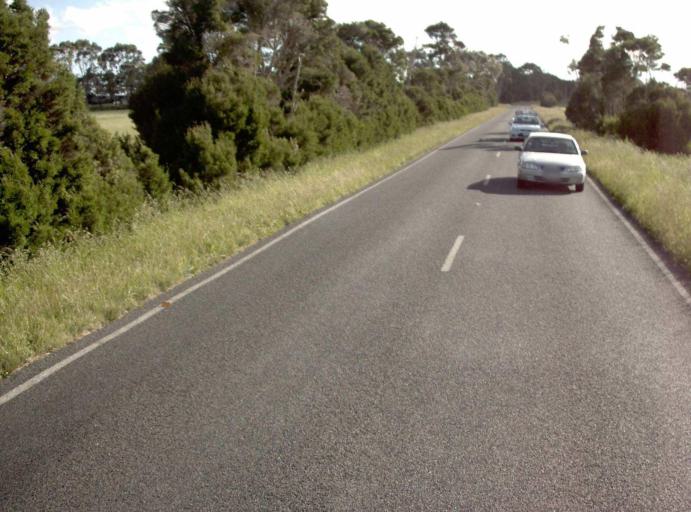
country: AU
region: Victoria
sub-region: Bass Coast
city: North Wonthaggi
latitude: -38.5250
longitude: 145.8877
